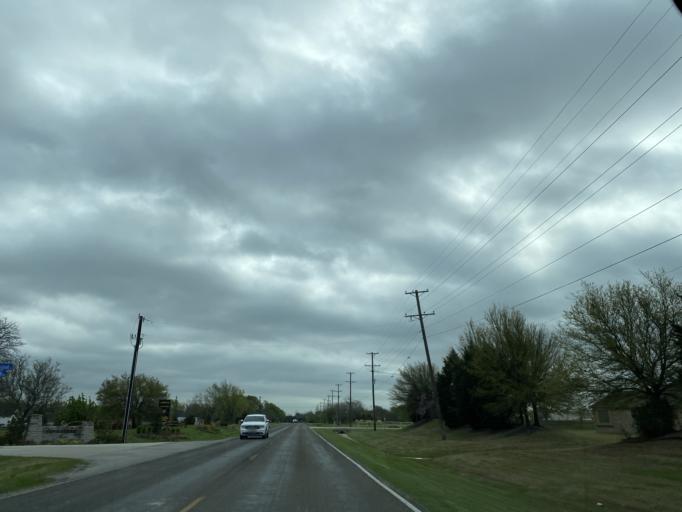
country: US
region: Texas
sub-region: Collin County
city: Lucas
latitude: 33.1001
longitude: -96.6049
